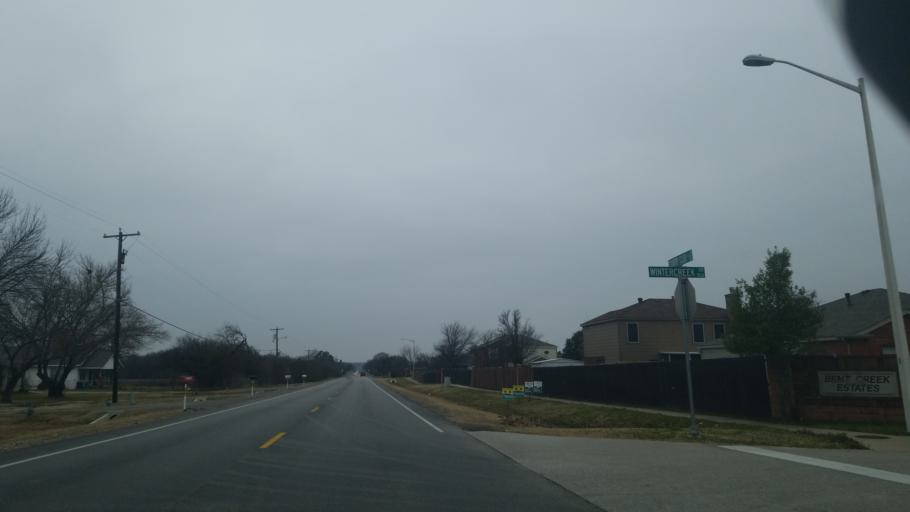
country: US
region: Texas
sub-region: Denton County
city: Denton
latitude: 33.1696
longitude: -97.1419
